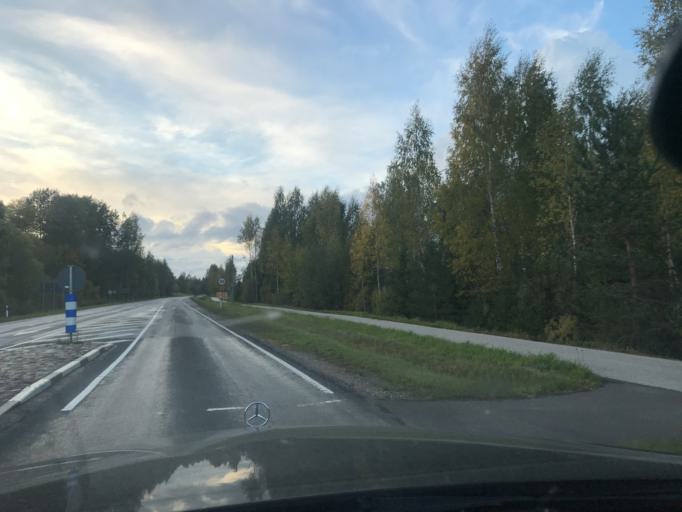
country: EE
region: Vorumaa
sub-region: Antsla vald
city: Vana-Antsla
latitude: 57.9267
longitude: 26.3320
